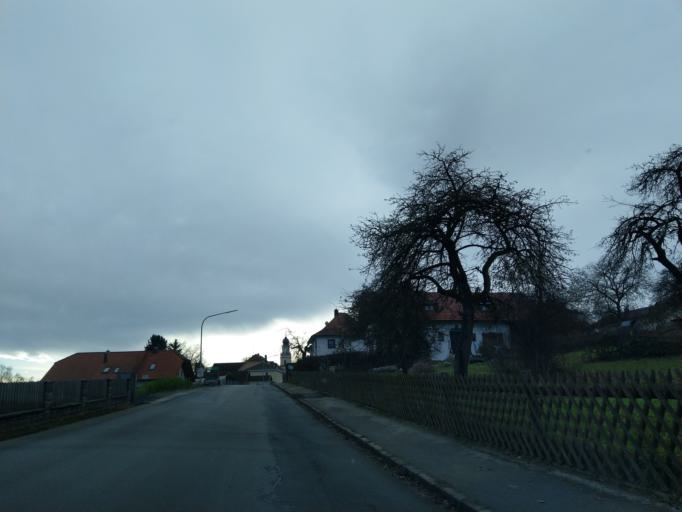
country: DE
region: Bavaria
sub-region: Lower Bavaria
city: Kunzing
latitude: 48.6367
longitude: 13.0284
